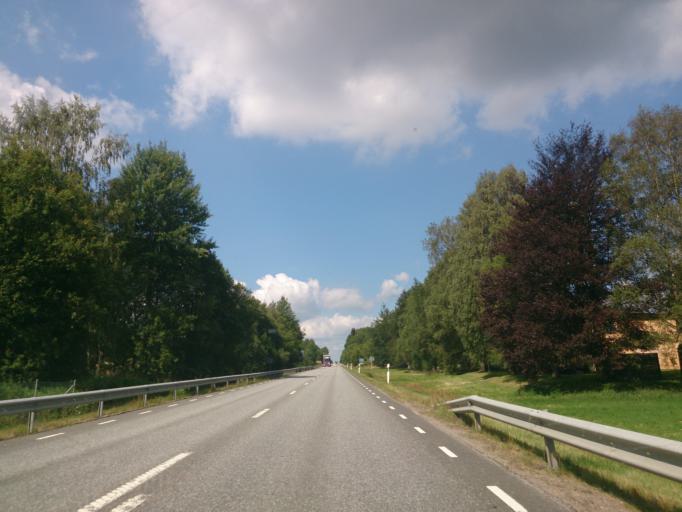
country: SE
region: Joenkoeping
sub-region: Varnamo Kommun
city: Bredaryd
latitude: 57.1725
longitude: 13.7360
